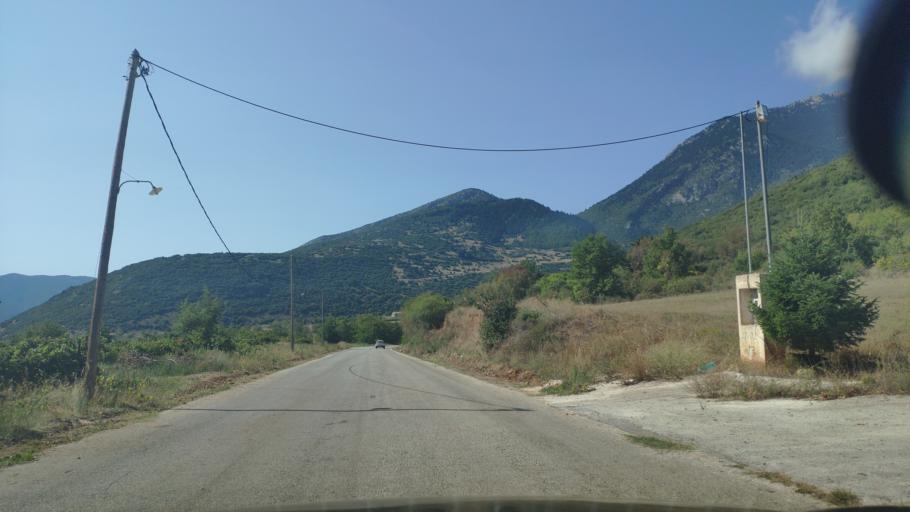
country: GR
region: Peloponnese
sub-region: Nomos Korinthias
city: Nemea
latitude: 37.9254
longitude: 22.5294
